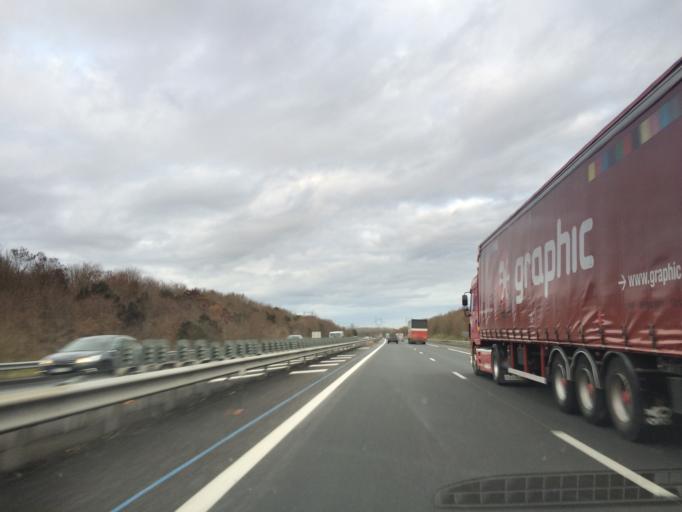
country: FR
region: Poitou-Charentes
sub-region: Departement des Deux-Sevres
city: Fors
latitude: 46.2414
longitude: -0.4330
